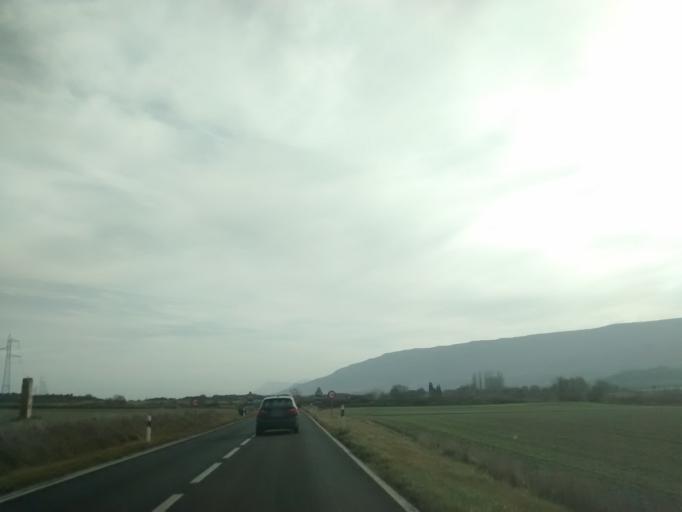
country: ES
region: Aragon
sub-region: Provincia de Zaragoza
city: Siguees
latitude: 42.6152
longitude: -1.0599
